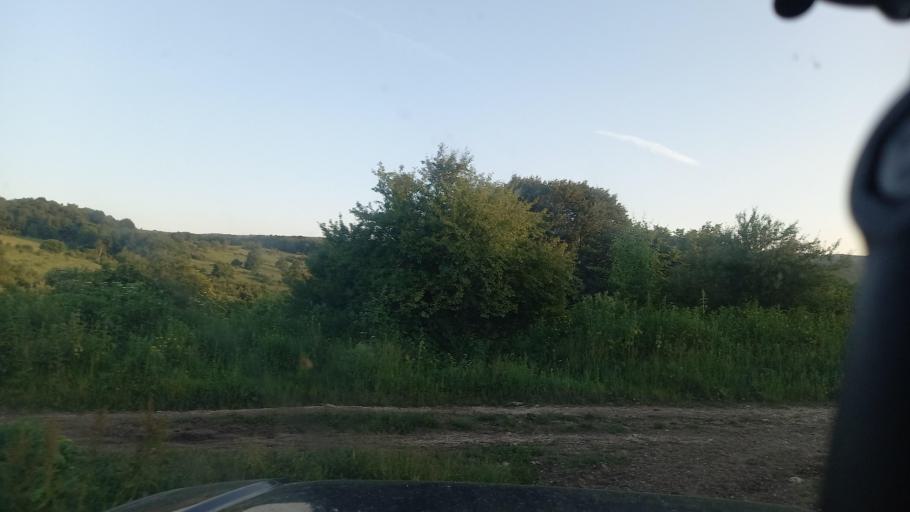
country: RU
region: Karachayevo-Cherkesiya
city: Pregradnaya
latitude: 44.1049
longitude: 41.1277
